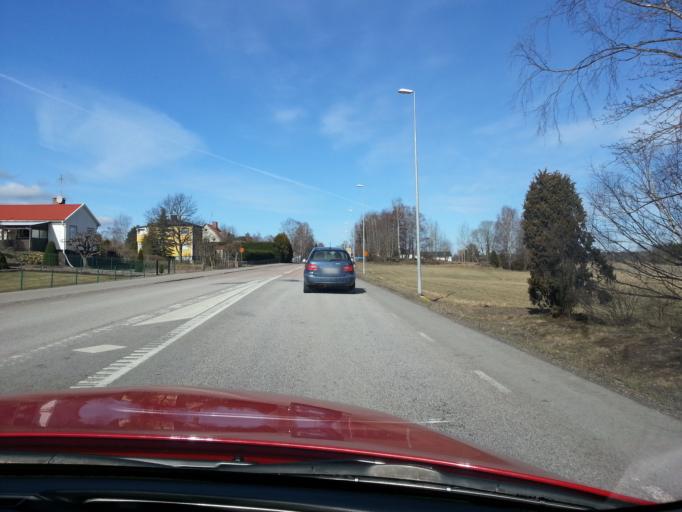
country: SE
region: Uppsala
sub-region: Osthammars Kommun
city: Gimo
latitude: 60.1658
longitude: 18.1937
